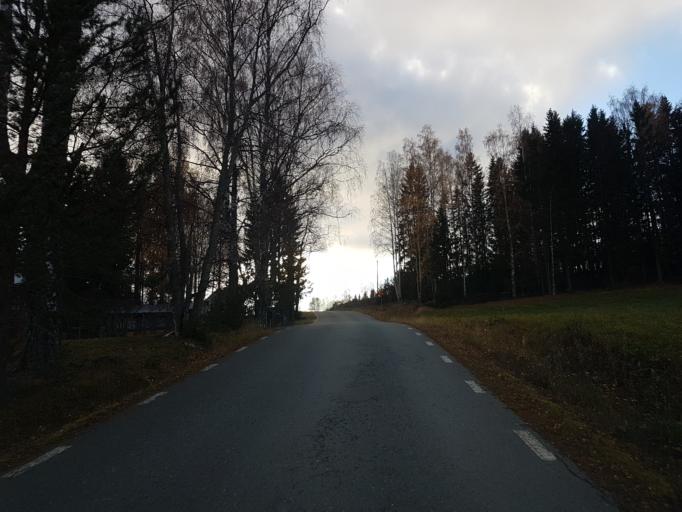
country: SE
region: Vaesternorrland
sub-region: Kramfors Kommun
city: Nordingra
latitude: 63.0634
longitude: 18.4120
